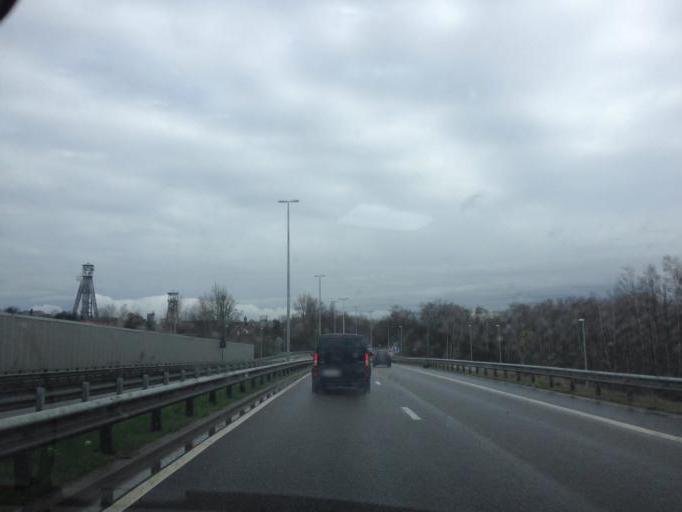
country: BE
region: Flanders
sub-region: Provincie Limburg
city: Genk
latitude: 50.9763
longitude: 5.4918
